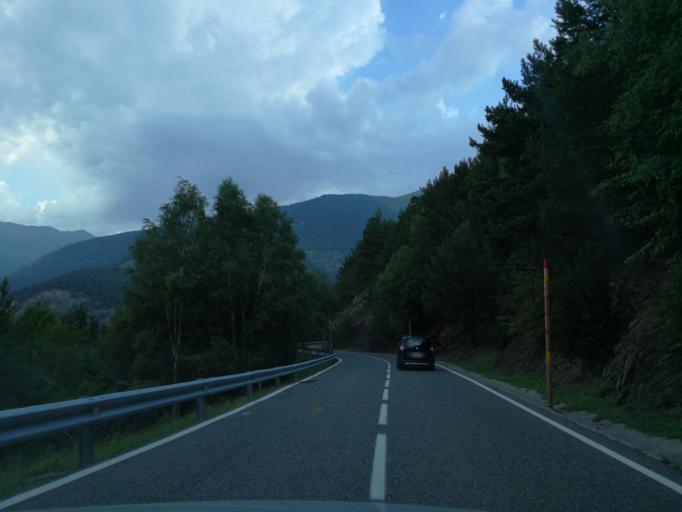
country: AD
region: Ordino
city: Ordino
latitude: 42.5515
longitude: 1.5437
